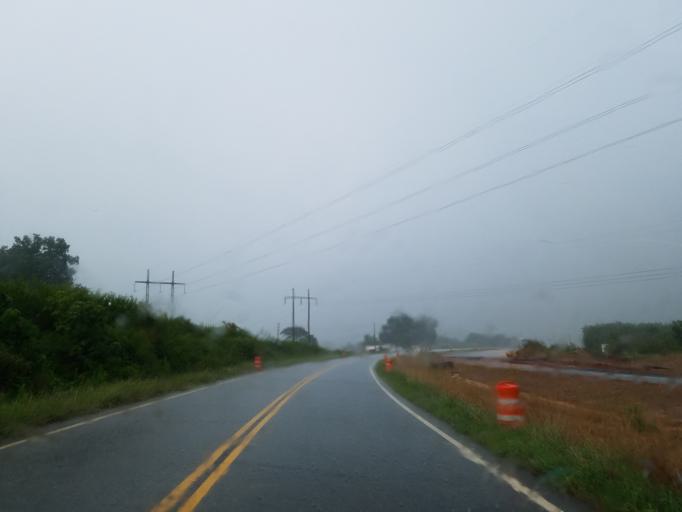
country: US
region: Georgia
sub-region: Floyd County
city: Shannon
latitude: 34.3669
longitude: -85.0447
